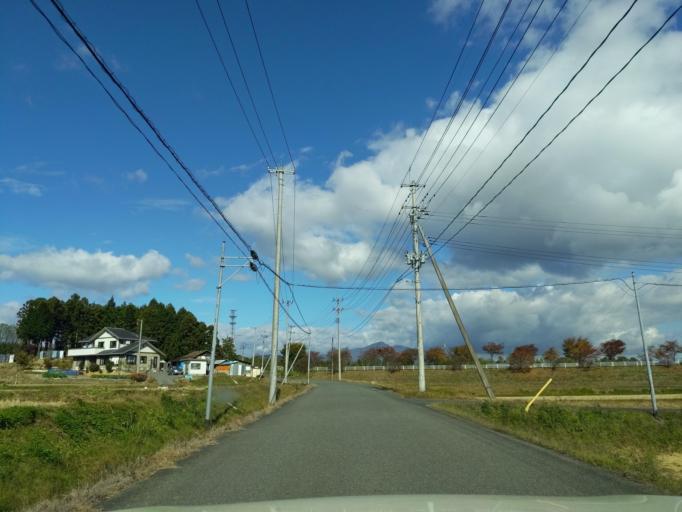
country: JP
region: Fukushima
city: Koriyama
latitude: 37.4461
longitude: 140.3245
